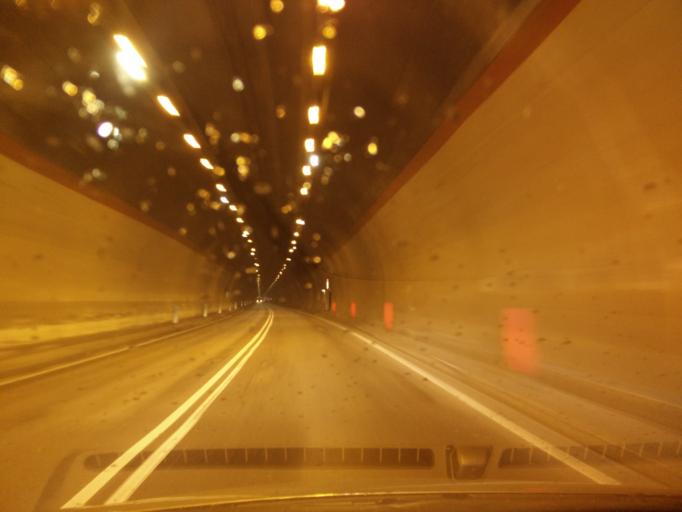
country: IT
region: Veneto
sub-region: Provincia di Belluno
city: Ospitale di Cadore
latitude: 46.3177
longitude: 12.3165
